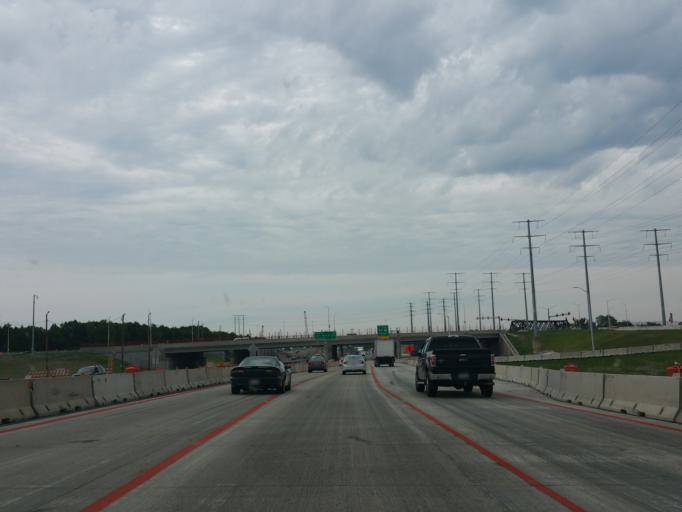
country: US
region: Wisconsin
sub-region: Waukesha County
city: Elm Grove
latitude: 43.0295
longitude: -88.0494
